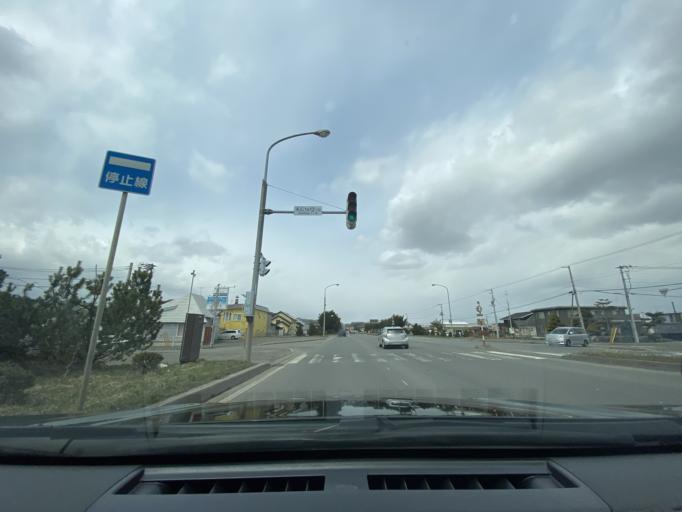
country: JP
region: Hokkaido
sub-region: Asahikawa-shi
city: Asahikawa
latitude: 43.8165
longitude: 142.4001
